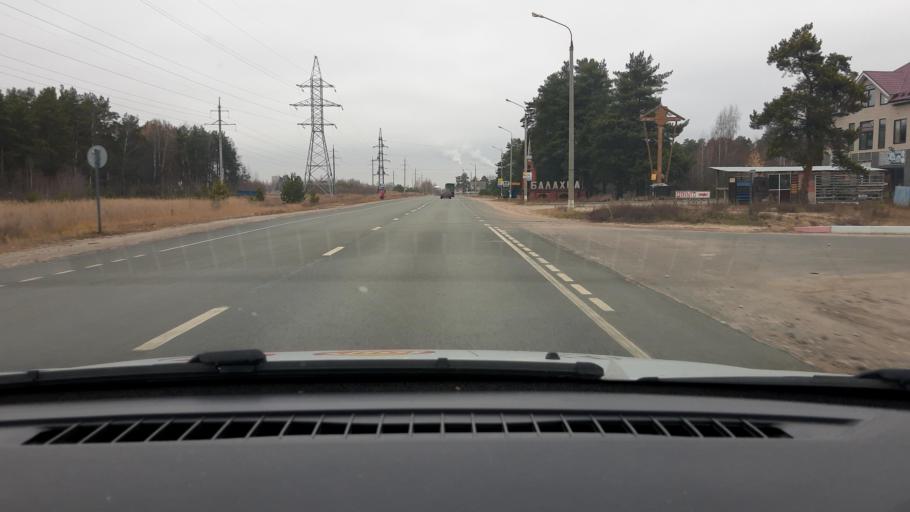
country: RU
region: Nizjnij Novgorod
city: Novaya Balakhna
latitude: 56.4711
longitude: 43.6130
